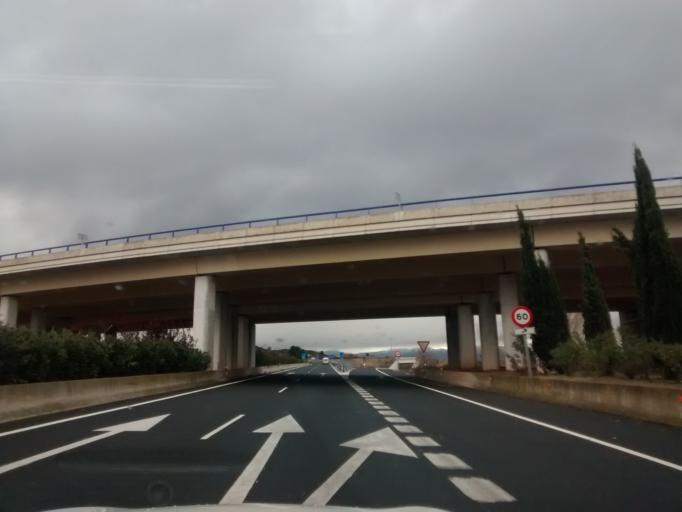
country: ES
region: La Rioja
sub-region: Provincia de La Rioja
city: Navarrete
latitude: 42.4440
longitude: -2.5452
